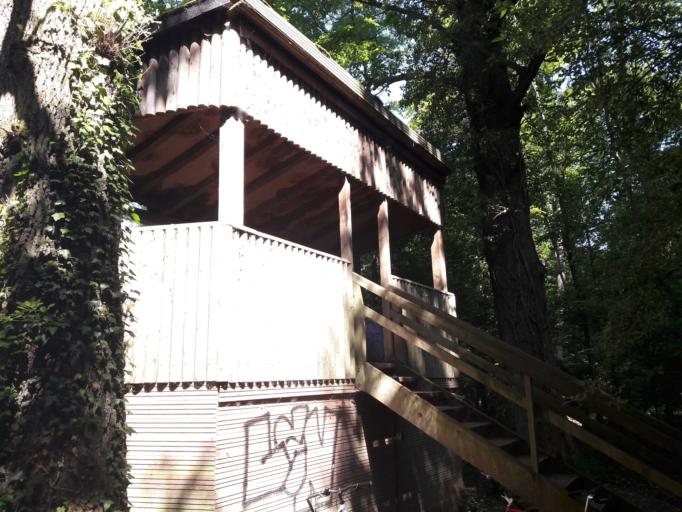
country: FR
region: Lorraine
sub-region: Departement de Meurthe-et-Moselle
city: Champenoux
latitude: 48.7688
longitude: 6.3360
